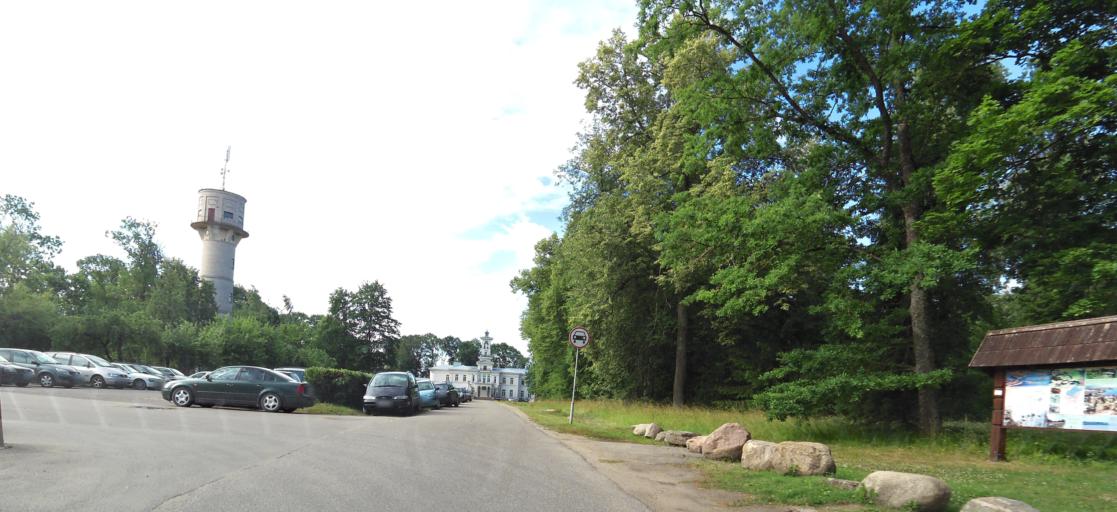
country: LT
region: Panevezys
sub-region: Birzai
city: Birzai
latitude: 56.2213
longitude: 24.7697
